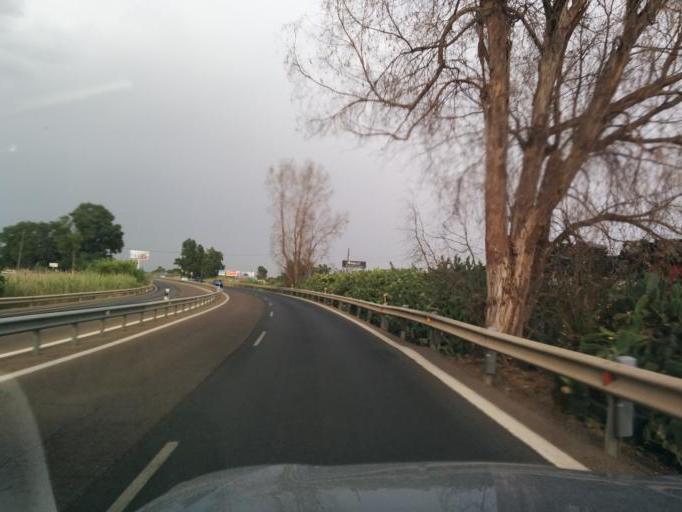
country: ES
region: Andalusia
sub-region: Provincia de Sevilla
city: Sevilla
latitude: 37.4138
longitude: -5.9372
